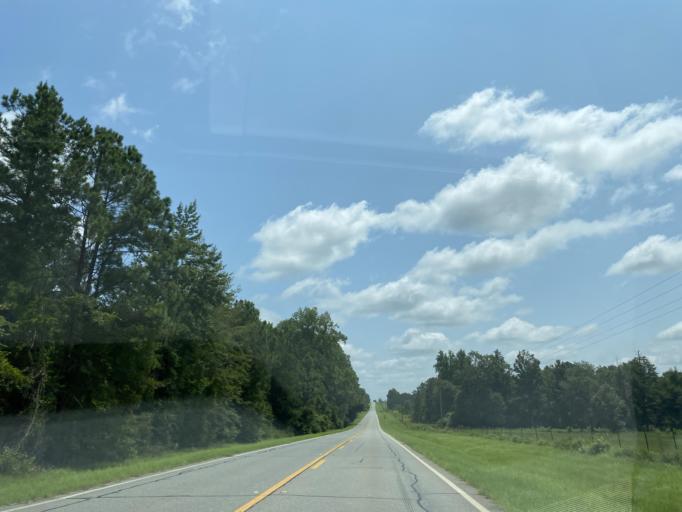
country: US
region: Georgia
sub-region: Wilcox County
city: Abbeville
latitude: 32.0097
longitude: -83.1119
